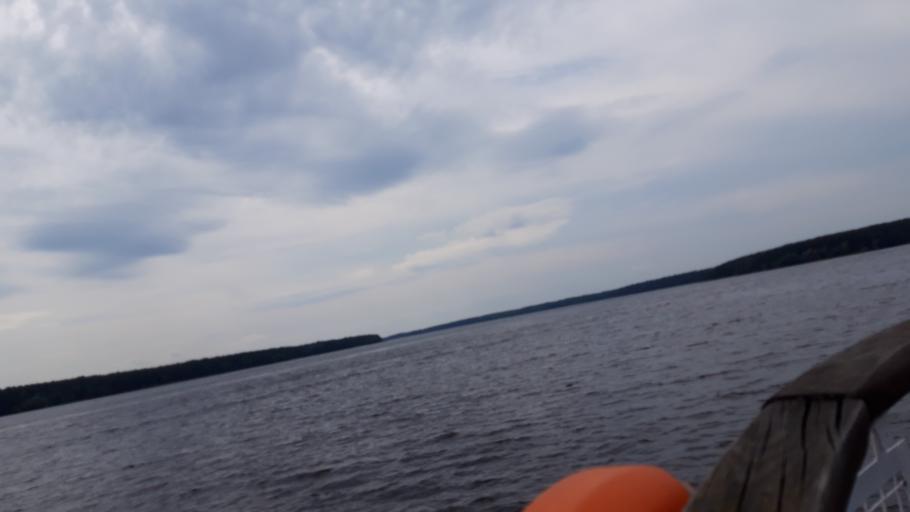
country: RU
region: Tverskaya
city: Konakovo
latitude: 56.7045
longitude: 36.7311
